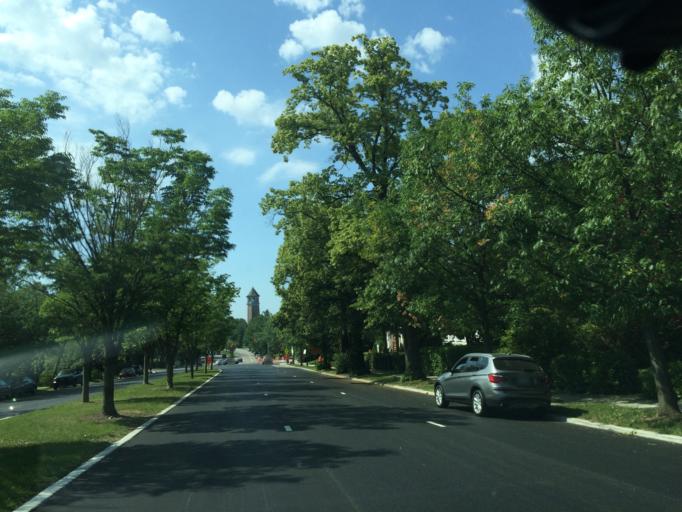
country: US
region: Maryland
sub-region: City of Baltimore
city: Baltimore
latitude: 39.3455
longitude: -76.6357
